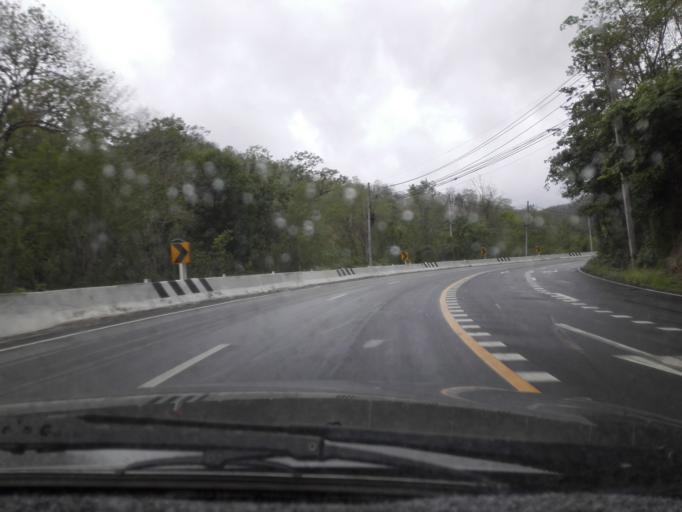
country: TH
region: Tak
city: Tak
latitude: 16.8105
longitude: 98.9806
